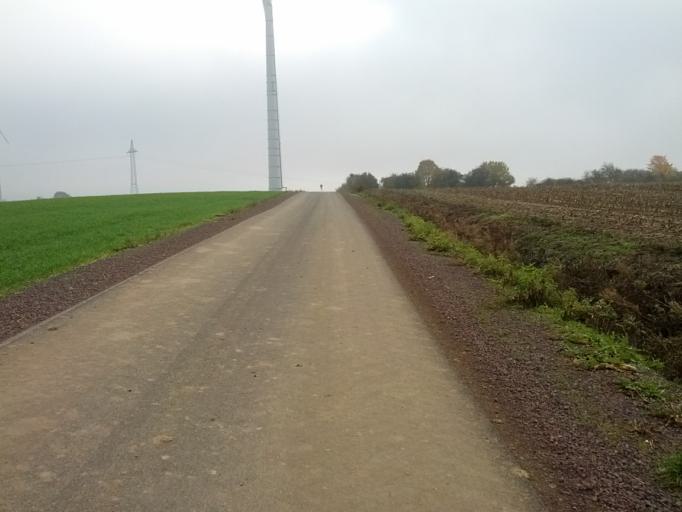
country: DE
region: Thuringia
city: Bischofroda
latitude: 51.0034
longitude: 10.3913
